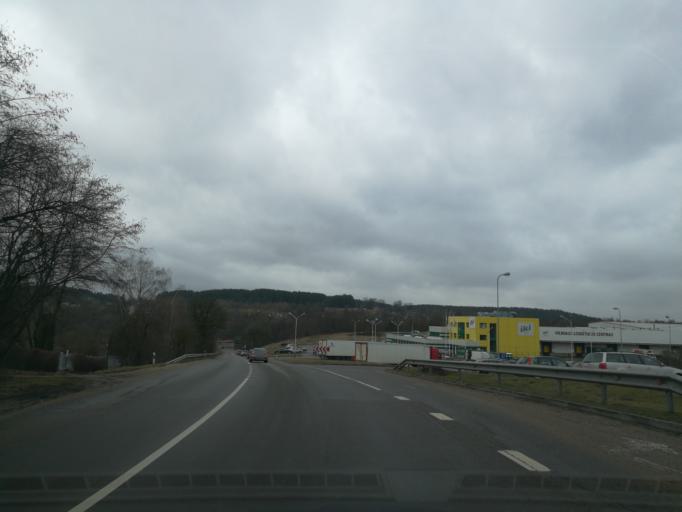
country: LT
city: Grigiskes
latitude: 54.6474
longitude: 25.1246
